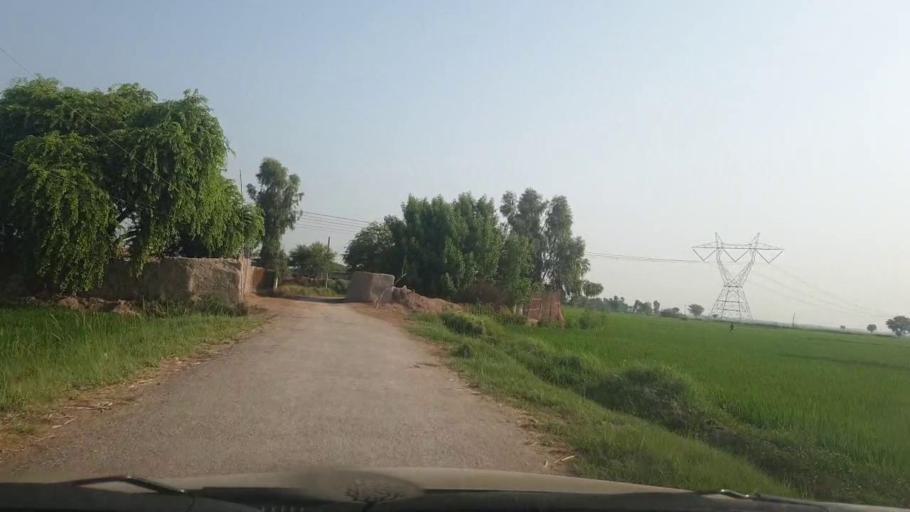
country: PK
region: Sindh
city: Larkana
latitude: 27.5908
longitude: 68.1605
